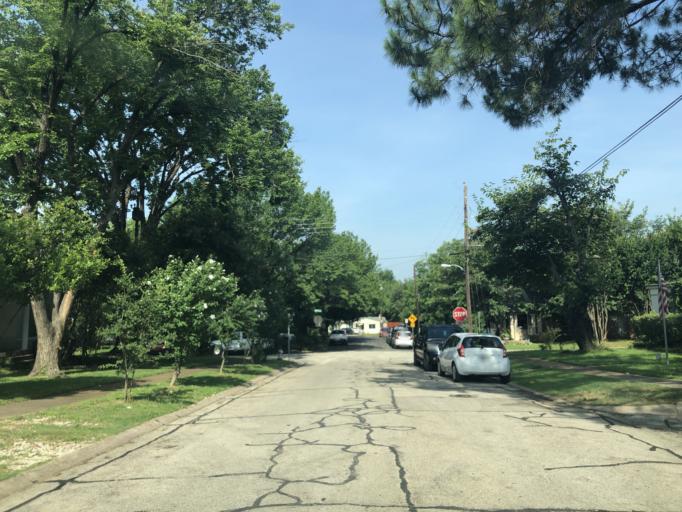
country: US
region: Texas
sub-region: Dallas County
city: Irving
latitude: 32.7985
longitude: -96.9529
